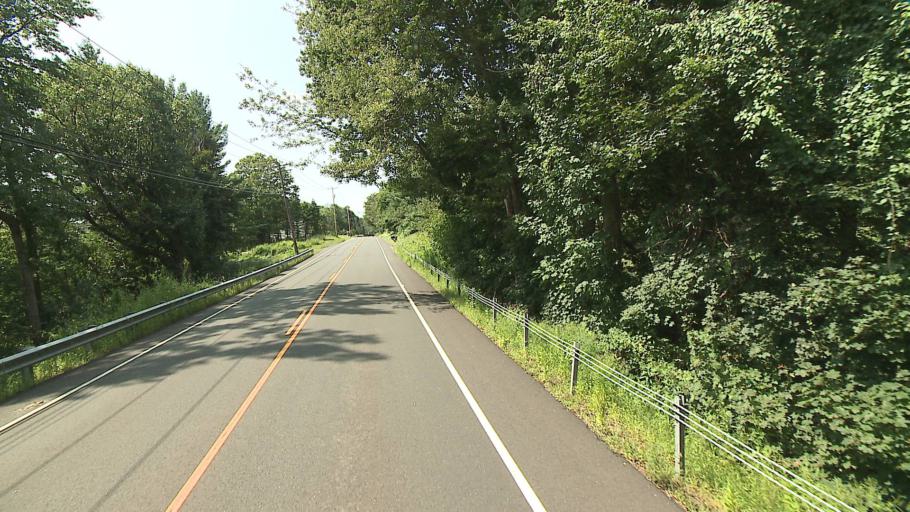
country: US
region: Connecticut
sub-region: Fairfield County
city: Shelton
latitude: 41.3343
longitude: -73.1582
